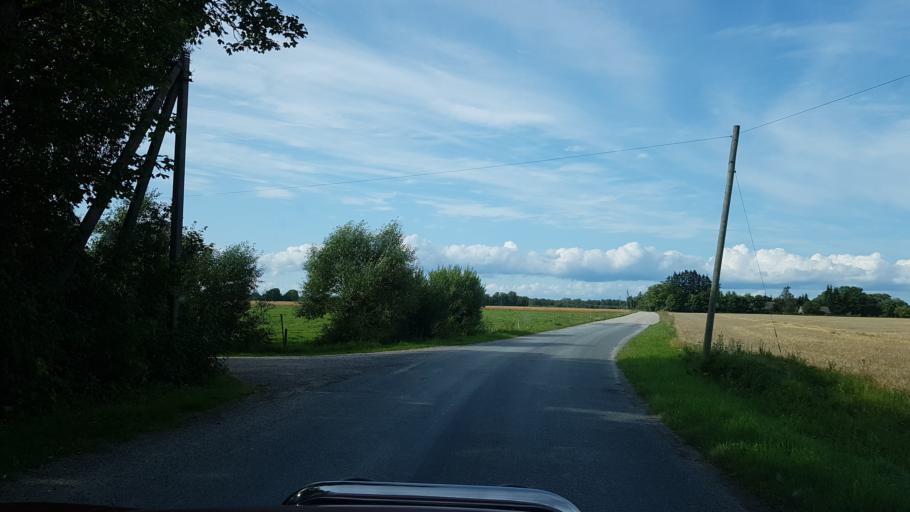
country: EE
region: Laeaene
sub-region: Lihula vald
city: Lihula
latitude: 58.4512
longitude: 23.9960
